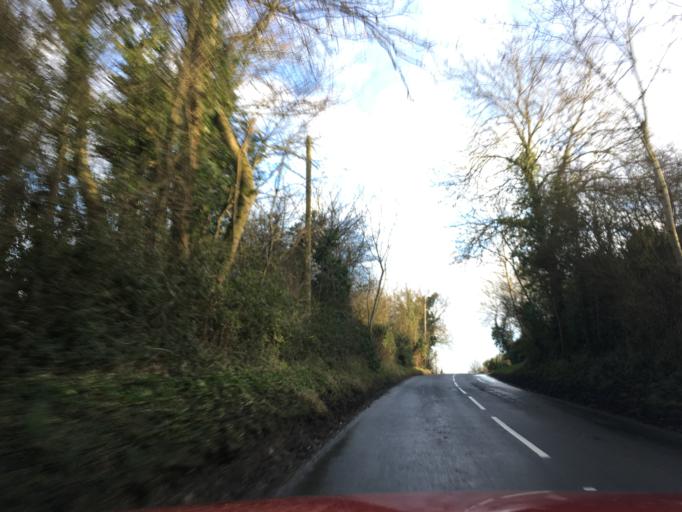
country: GB
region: England
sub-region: Warwickshire
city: Henley in Arden
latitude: 52.2256
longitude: -1.7764
